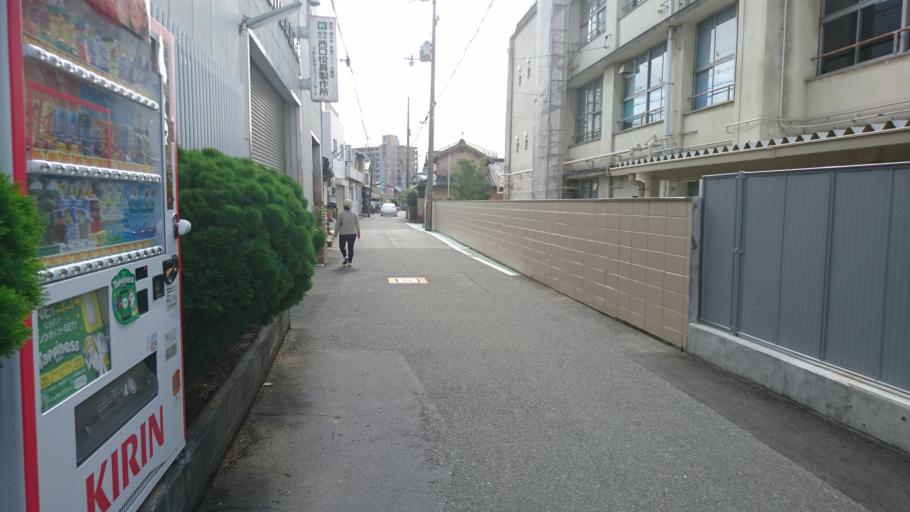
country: JP
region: Osaka
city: Moriguchi
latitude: 34.7090
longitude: 135.5862
